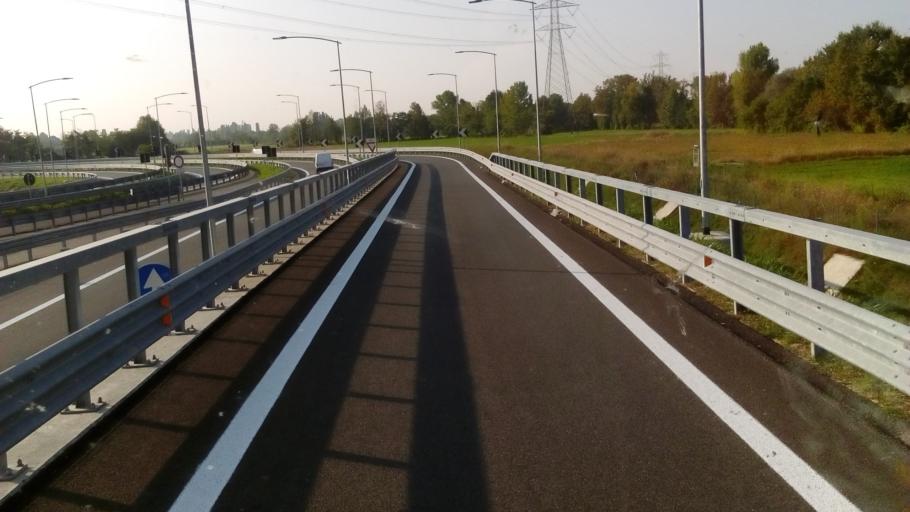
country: IT
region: Lombardy
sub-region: Provincia di Bergamo
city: Casirate d'Adda
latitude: 45.5075
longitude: 9.5507
